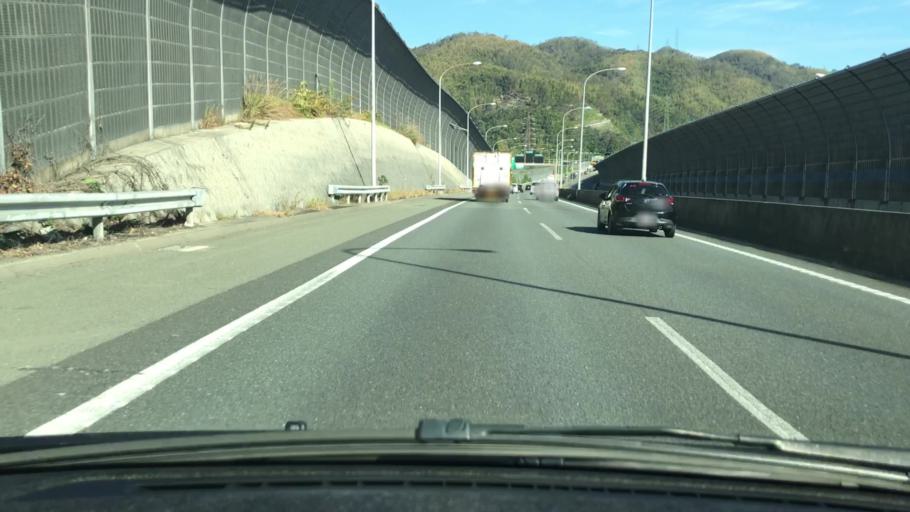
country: JP
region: Kyoto
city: Yawata
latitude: 34.8866
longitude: 135.6615
